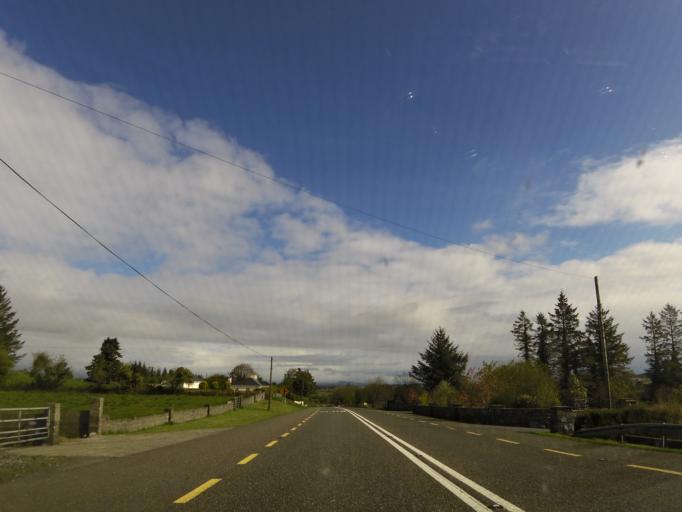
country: IE
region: Connaught
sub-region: Sligo
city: Tobercurry
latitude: 53.9230
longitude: -8.7849
